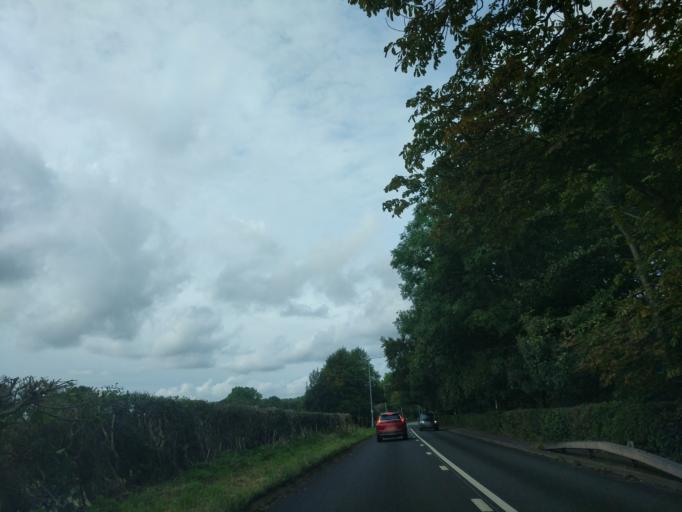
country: GB
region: England
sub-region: Staffordshire
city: Audley
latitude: 53.0068
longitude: -2.3213
